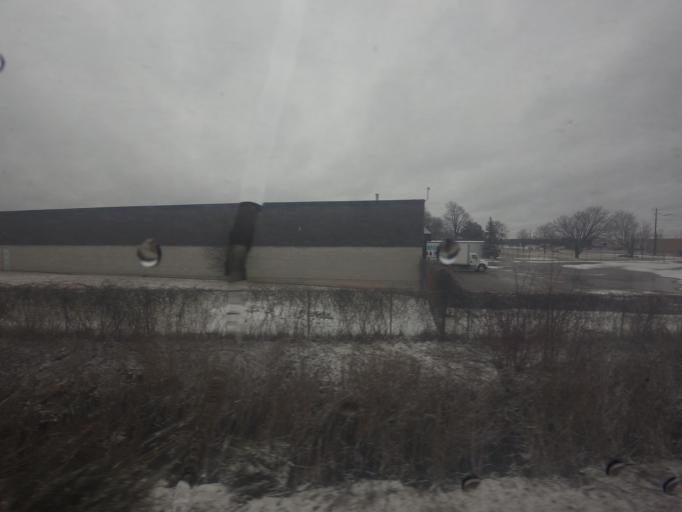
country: CA
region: Ontario
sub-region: Lanark County
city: Smiths Falls
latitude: 44.8986
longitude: -76.0056
